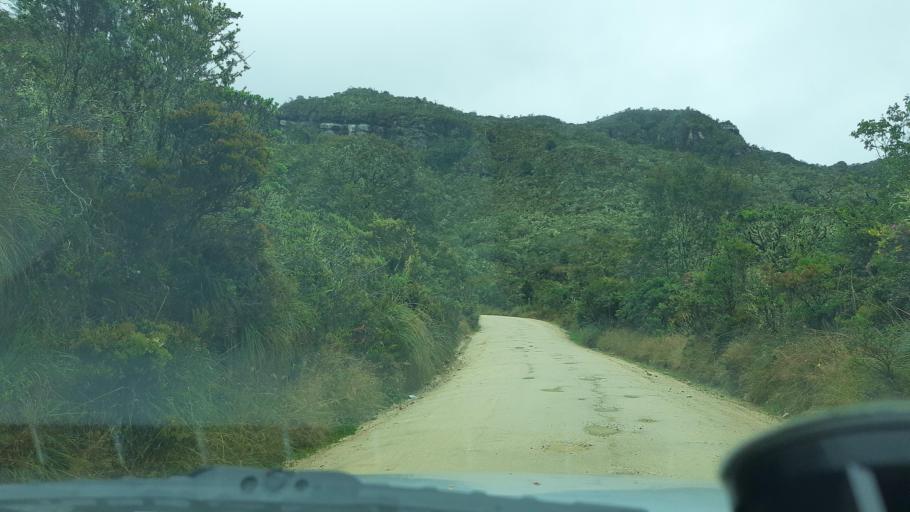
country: CO
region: Cundinamarca
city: Villapinzon
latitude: 5.2066
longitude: -73.5502
